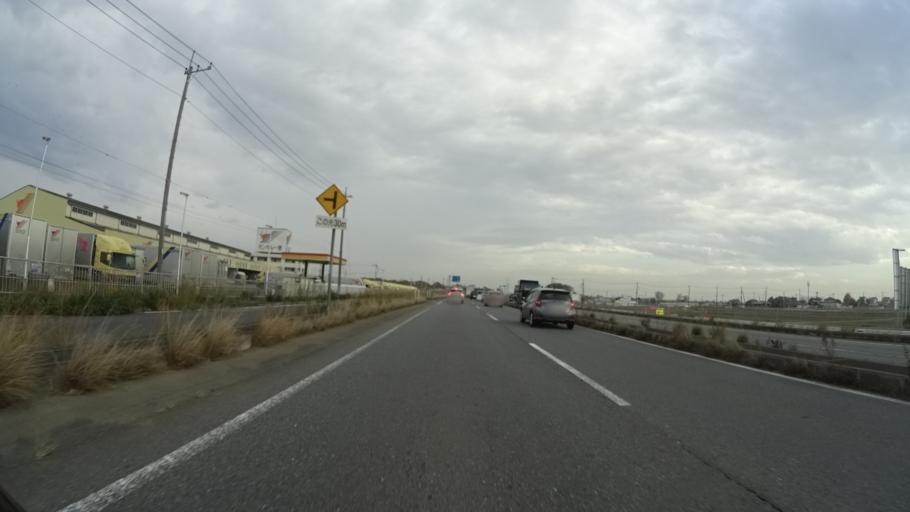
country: JP
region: Gunma
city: Isesaki
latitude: 36.3642
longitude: 139.1824
